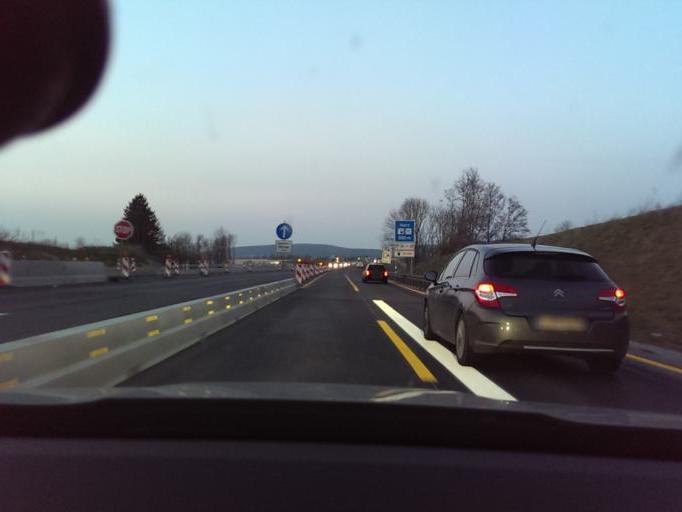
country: DE
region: Lower Saxony
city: Seesen
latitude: 51.9180
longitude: 10.1369
